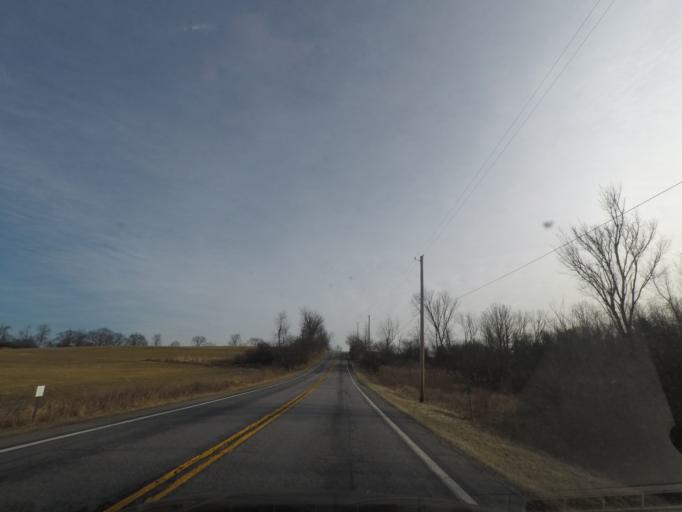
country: US
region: New York
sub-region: Saratoga County
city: Stillwater
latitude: 42.9856
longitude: -73.6535
